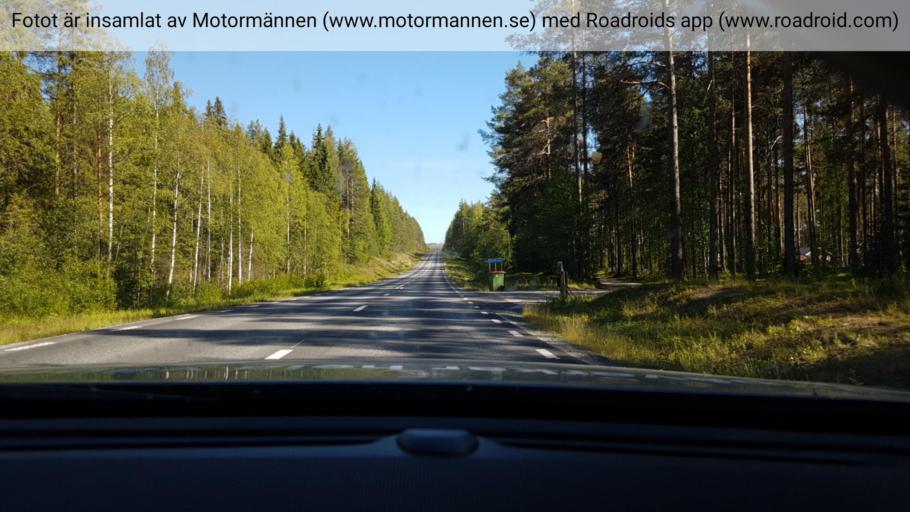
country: SE
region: Vaesterbotten
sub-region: Lycksele Kommun
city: Lycksele
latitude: 64.5453
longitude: 18.7453
